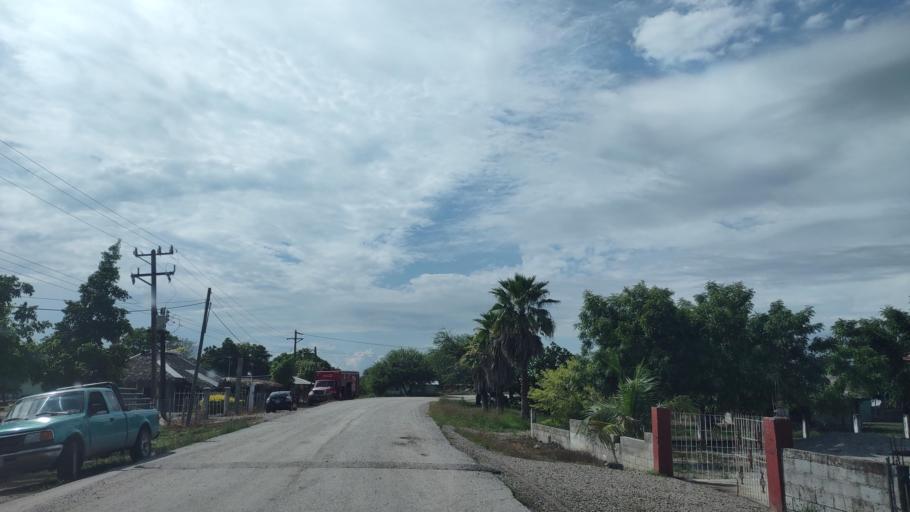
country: MX
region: Veracruz
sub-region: Panuco
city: Oviedo
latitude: 22.0036
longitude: -98.4605
